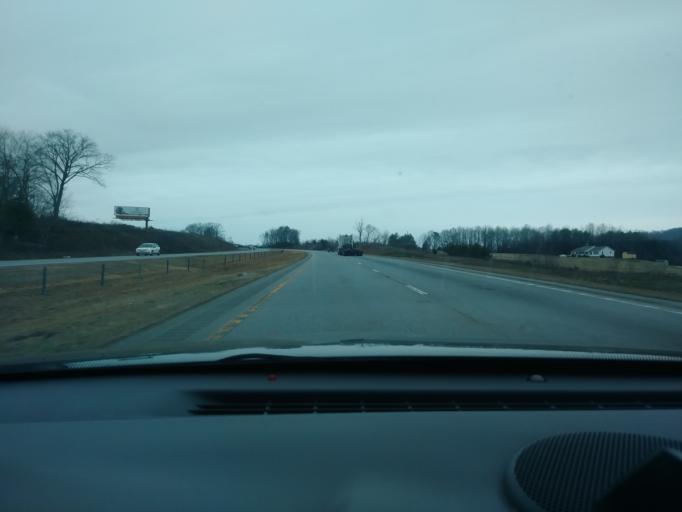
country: US
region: North Carolina
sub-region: Yadkin County
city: Jonesville
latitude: 36.1397
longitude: -80.8678
